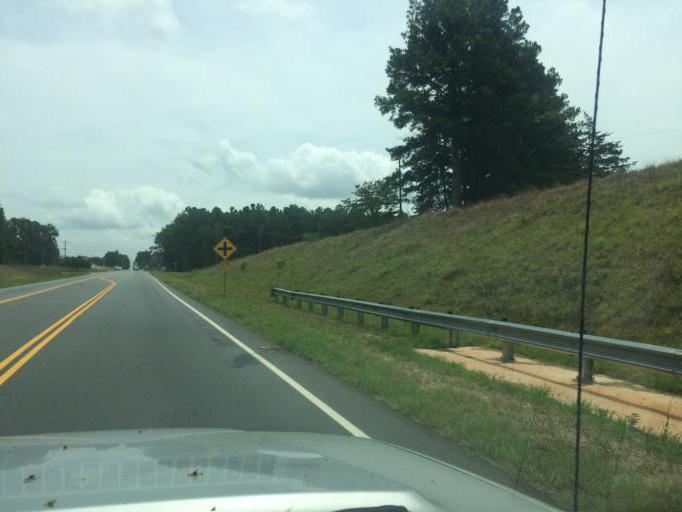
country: US
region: South Carolina
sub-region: Anderson County
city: Centerville
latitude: 34.5223
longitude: -82.7776
